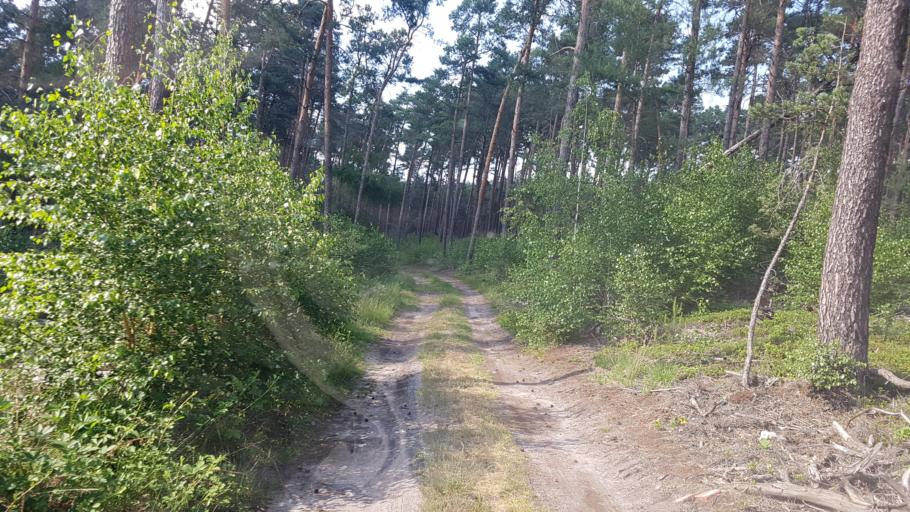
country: DE
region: Brandenburg
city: Trobitz
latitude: 51.6413
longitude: 13.4164
